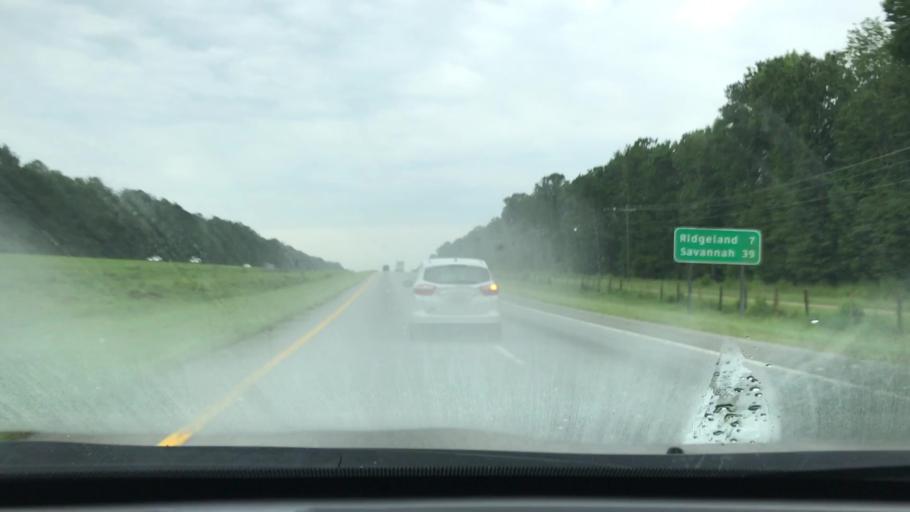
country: US
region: South Carolina
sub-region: Jasper County
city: Ridgeland
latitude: 32.5696
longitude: -80.9394
